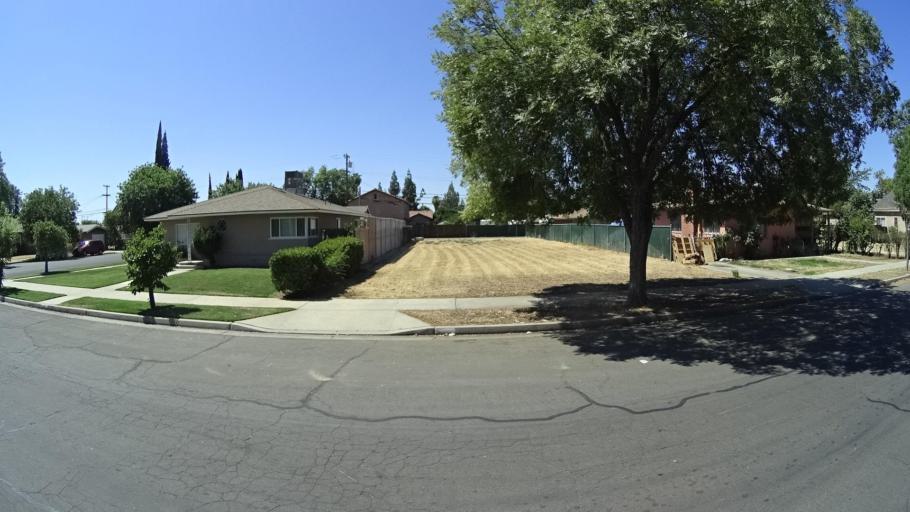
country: US
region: California
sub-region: Fresno County
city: Fresno
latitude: 36.7370
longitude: -119.7663
